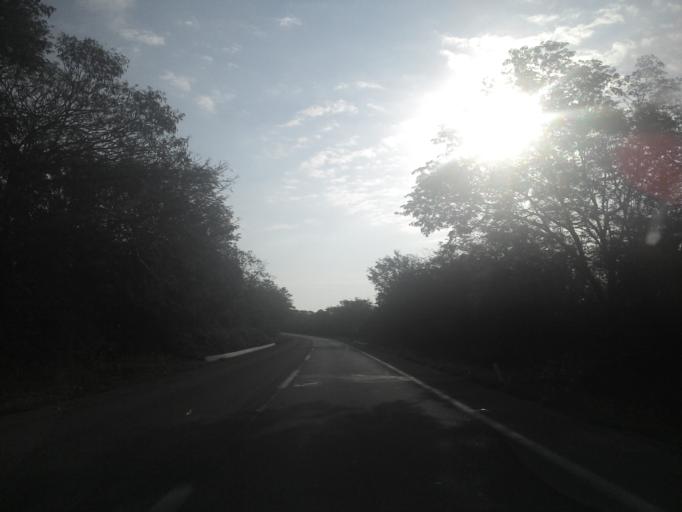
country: MX
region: Yucatan
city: Tinum
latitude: 20.7080
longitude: -88.4591
